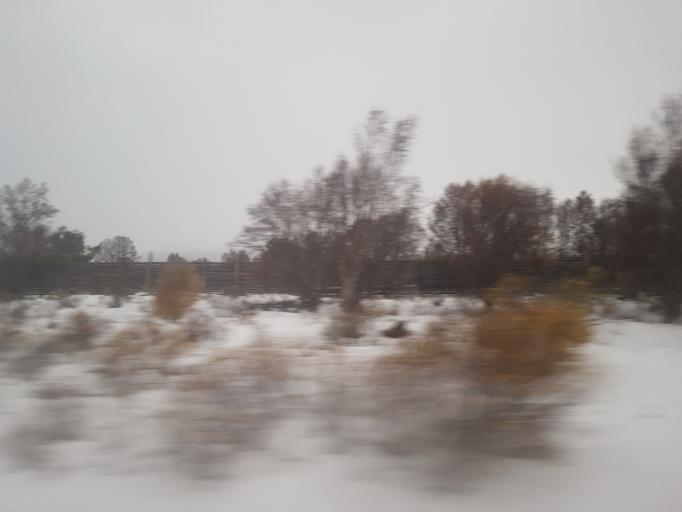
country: NO
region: Oppland
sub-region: Dovre
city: Dovre
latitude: 62.1088
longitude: 9.2500
